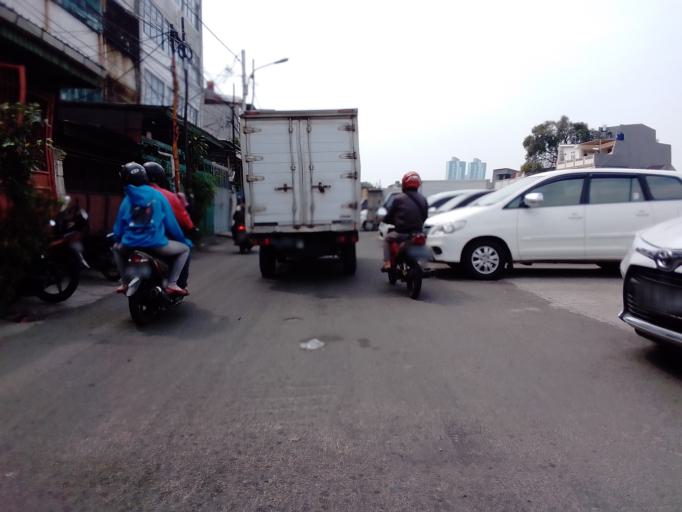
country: ID
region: Jakarta Raya
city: Jakarta
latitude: -6.1595
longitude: 106.8107
